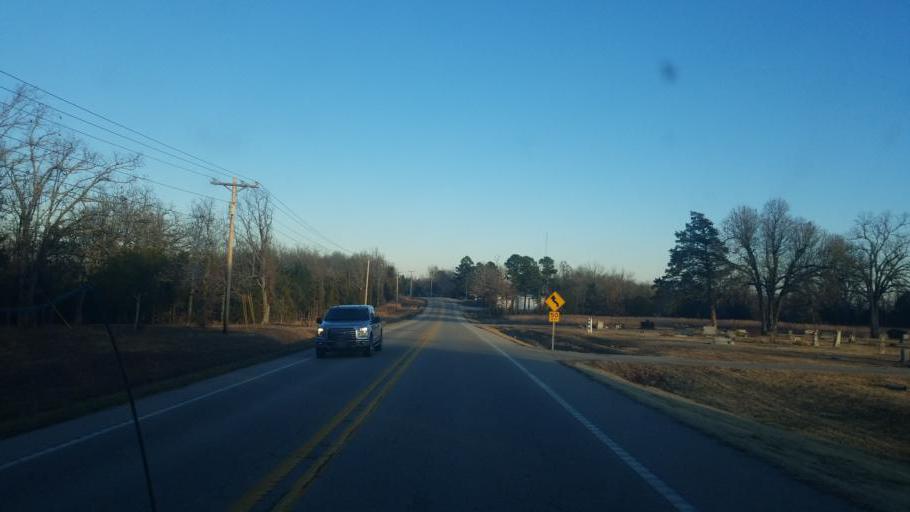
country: US
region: Arkansas
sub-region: Baxter County
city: Mountain Home
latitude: 36.3837
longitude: -92.1719
